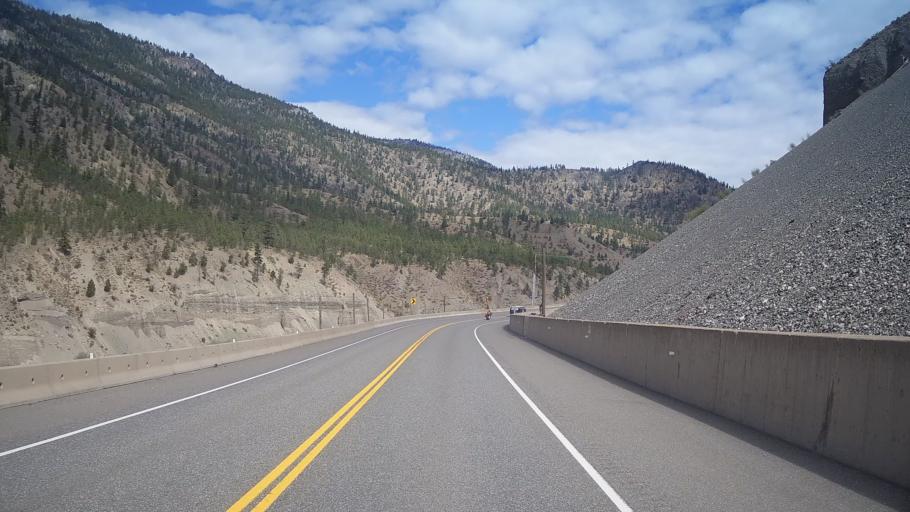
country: CA
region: British Columbia
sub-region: Thompson-Nicola Regional District
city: Ashcroft
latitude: 50.2784
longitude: -121.4056
